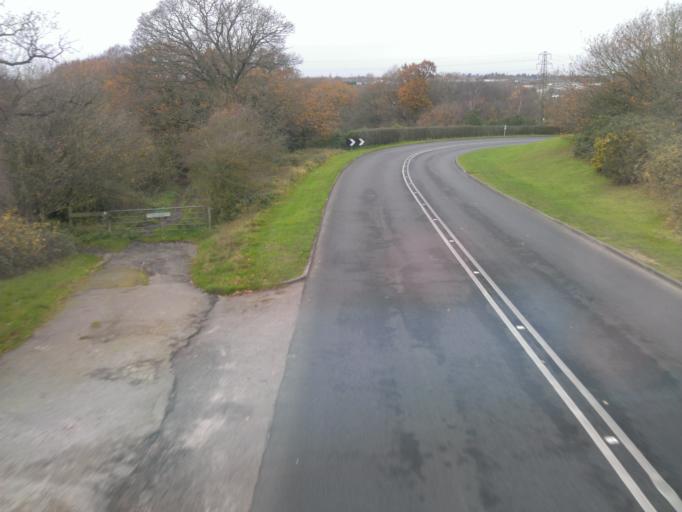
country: GB
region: England
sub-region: Essex
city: Rowhedge
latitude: 51.8733
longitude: 0.9445
